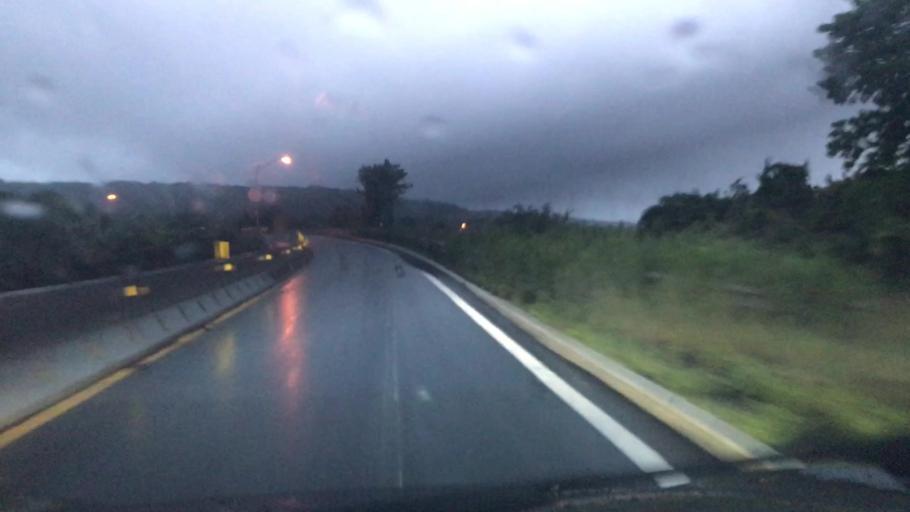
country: US
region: New Jersey
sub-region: Somerset County
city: Bedminster
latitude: 40.6413
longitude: -74.6487
